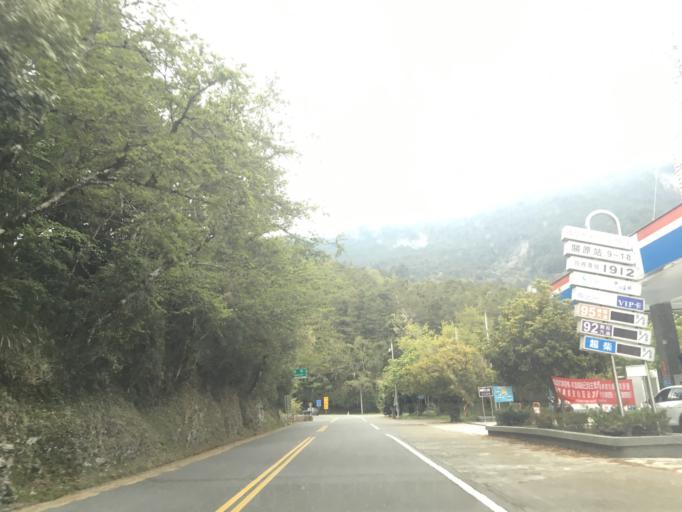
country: TW
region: Taiwan
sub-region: Hualien
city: Hualian
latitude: 24.1848
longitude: 121.3421
